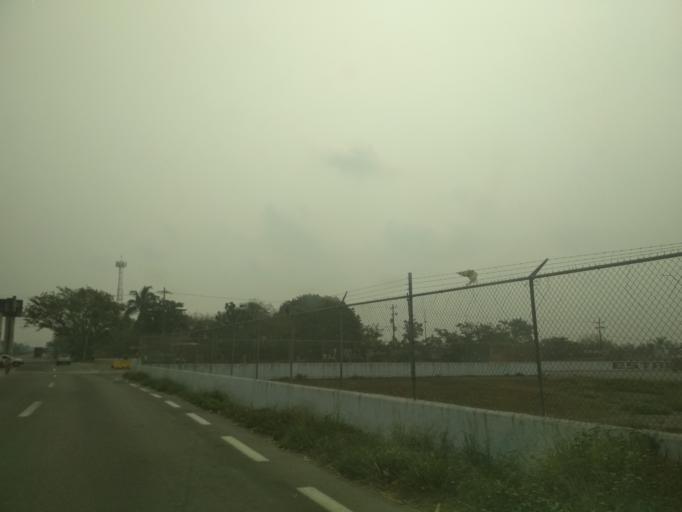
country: MX
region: Veracruz
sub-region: Veracruz
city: Delfino Victoria (Santa Fe)
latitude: 19.2023
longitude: -96.2684
